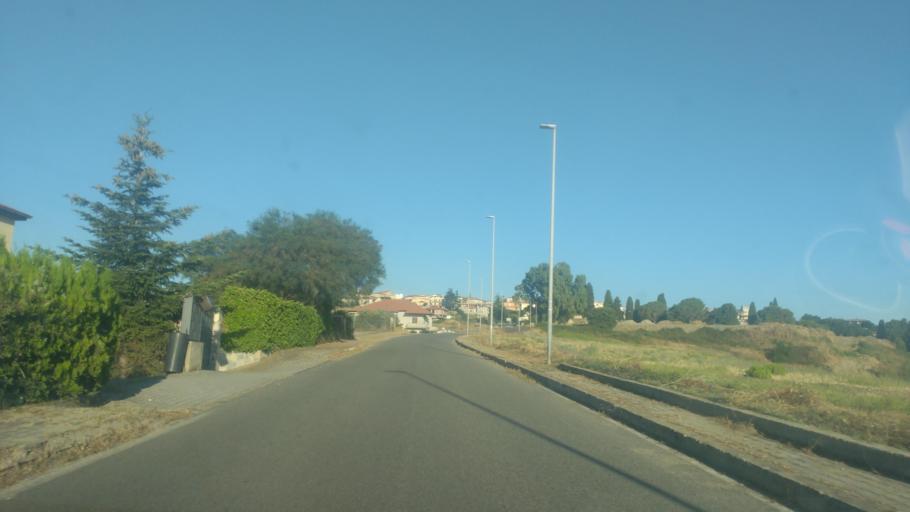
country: IT
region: Calabria
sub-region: Provincia di Catanzaro
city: Staletti
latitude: 38.7649
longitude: 16.5492
